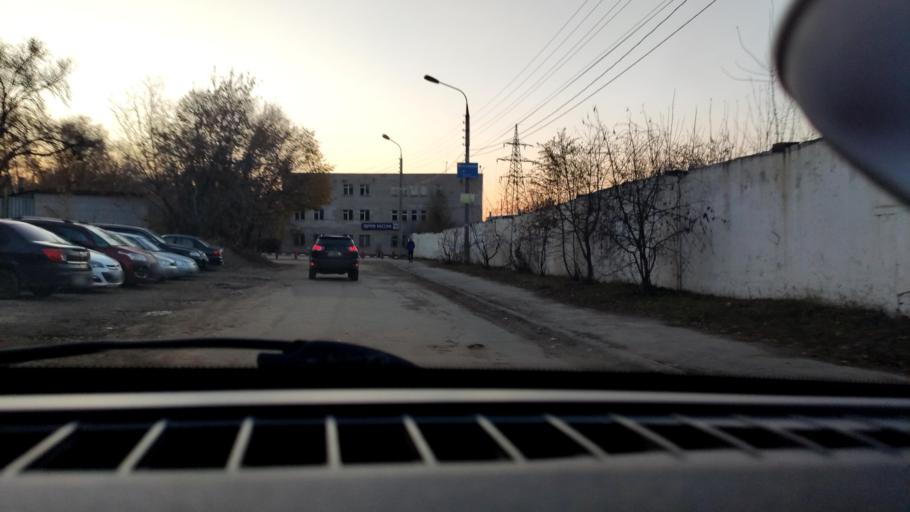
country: RU
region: Samara
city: Samara
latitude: 53.1810
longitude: 50.1115
